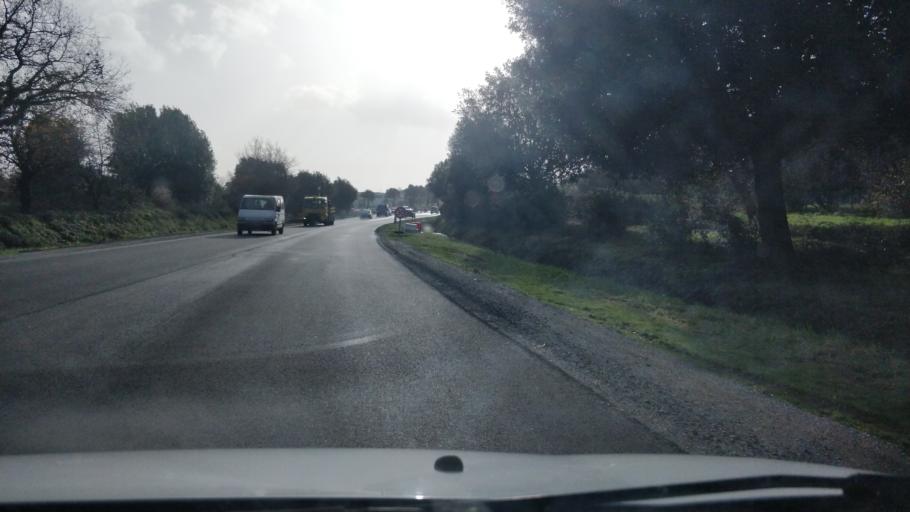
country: FR
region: Pays de la Loire
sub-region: Departement de la Loire-Atlantique
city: Guerande
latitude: 47.3314
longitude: -2.4173
